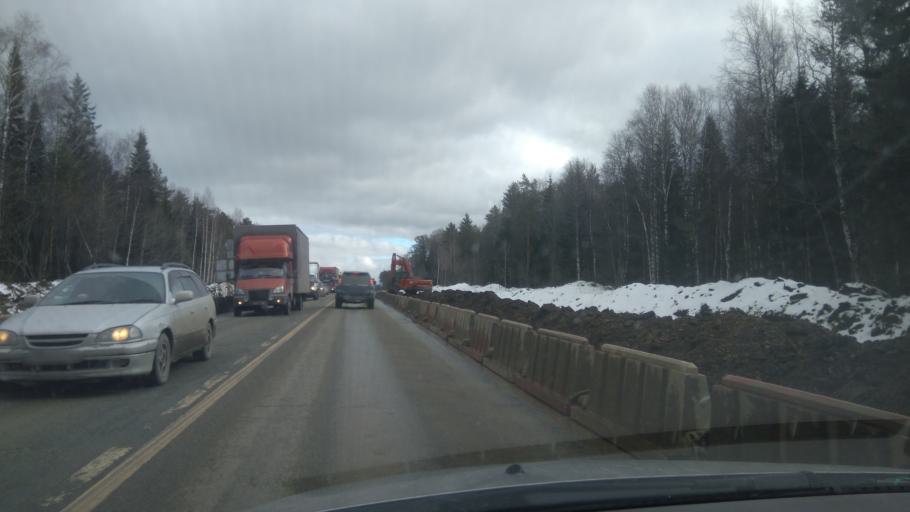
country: RU
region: Sverdlovsk
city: Bisert'
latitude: 56.8332
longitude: 58.9417
